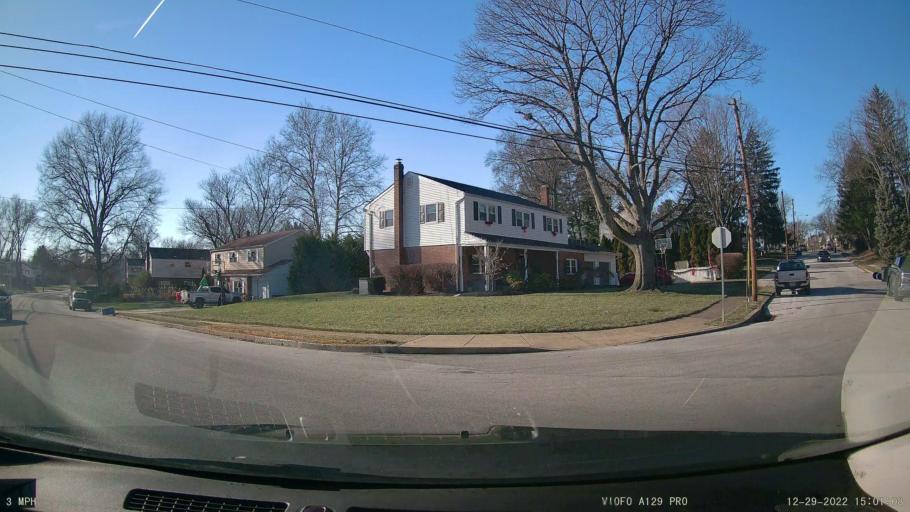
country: US
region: Pennsylvania
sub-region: Montgomery County
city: Blue Bell
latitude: 40.1345
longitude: -75.2986
